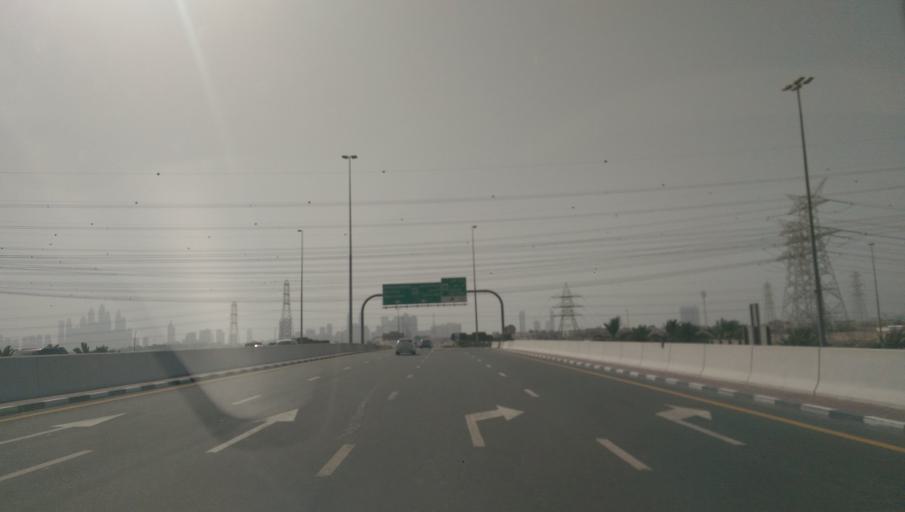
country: AE
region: Dubai
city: Dubai
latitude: 25.0766
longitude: 55.2109
